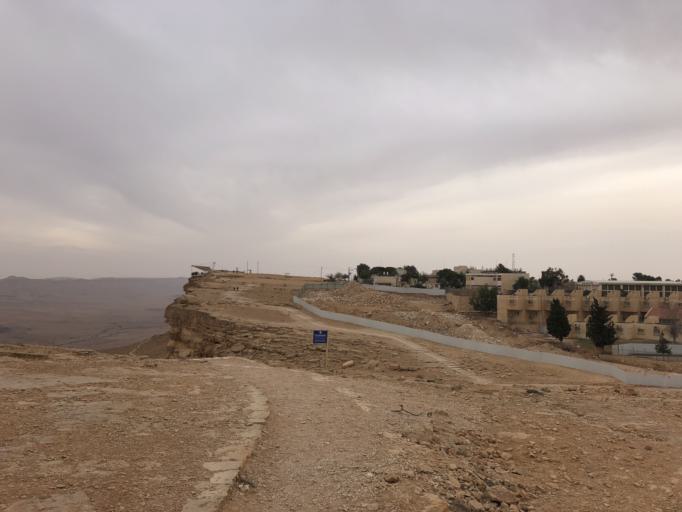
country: IL
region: Southern District
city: Mitzpe Ramon
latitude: 30.6080
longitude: 34.8062
